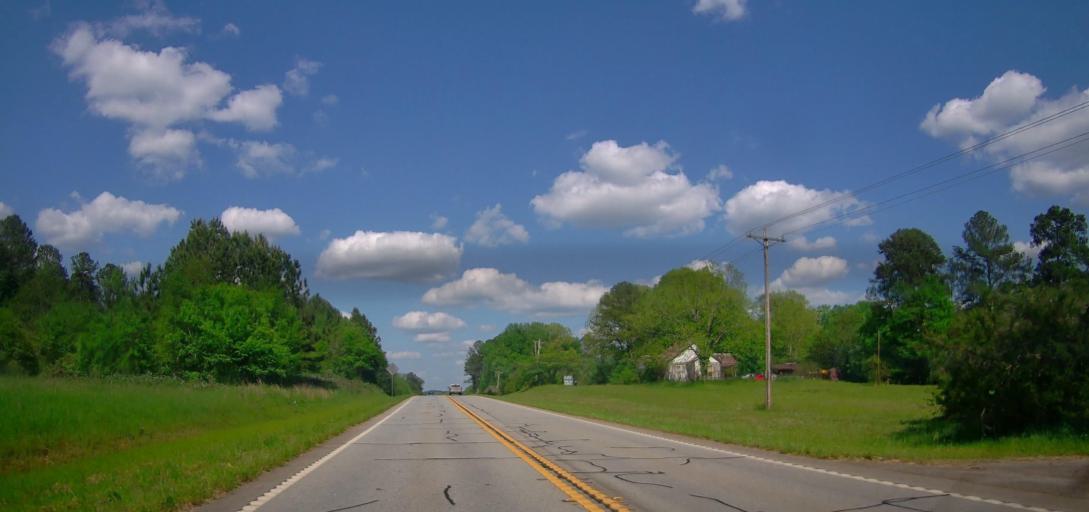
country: US
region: Georgia
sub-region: Greene County
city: Greensboro
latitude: 33.5734
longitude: -83.2202
